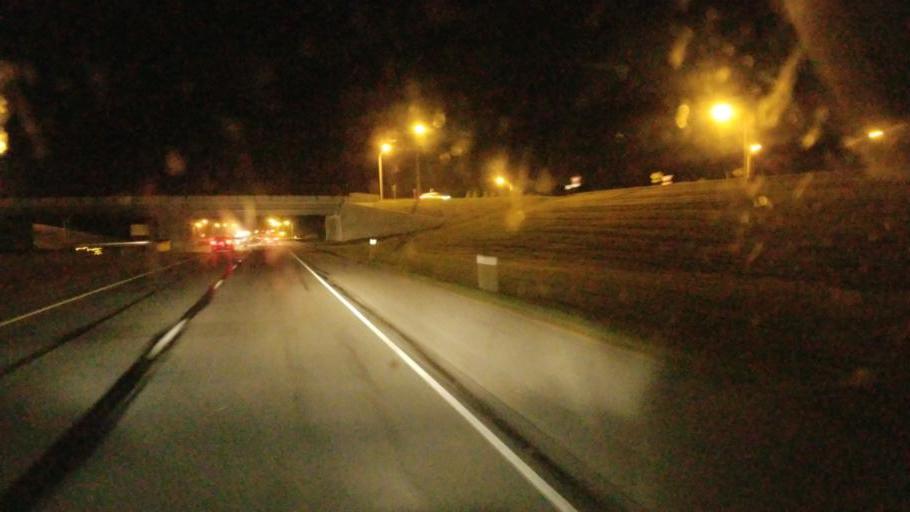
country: US
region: Indiana
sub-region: Allen County
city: Fort Wayne
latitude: 41.1990
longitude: -85.1040
